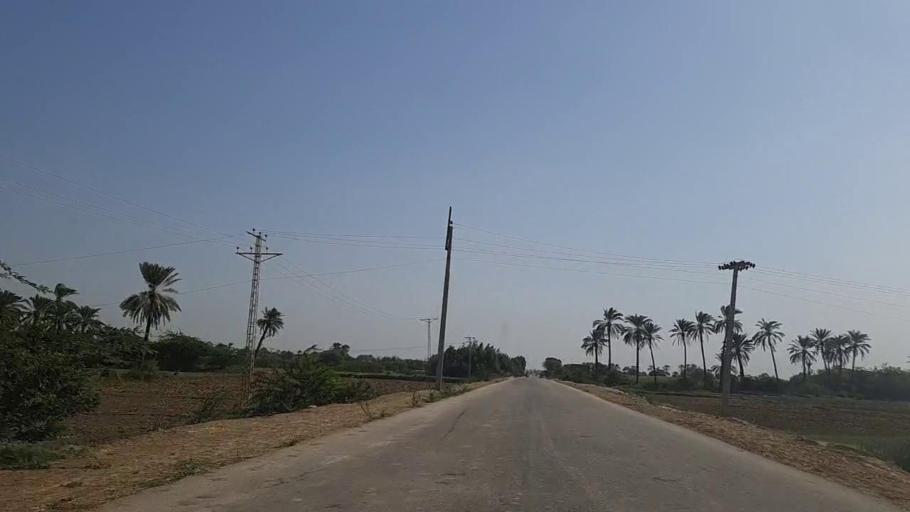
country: PK
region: Sindh
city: Mirpur Batoro
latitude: 24.7611
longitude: 68.2208
